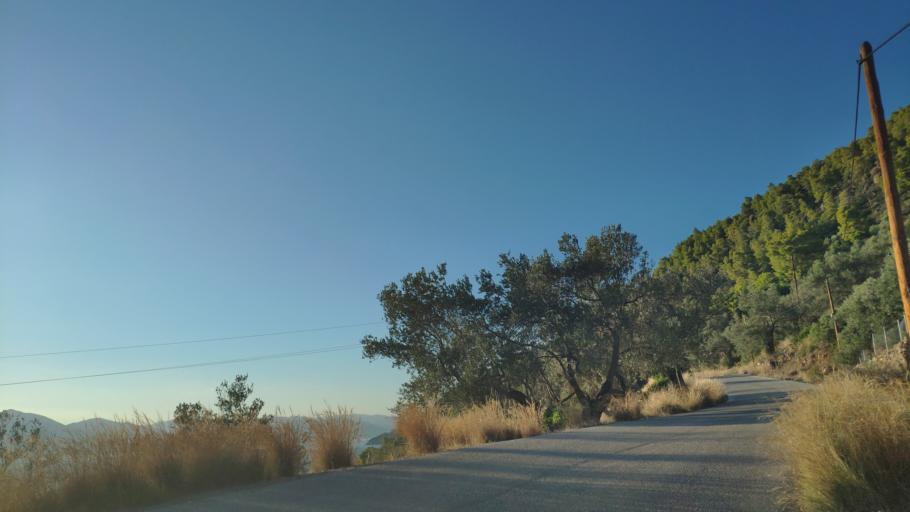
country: GR
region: Attica
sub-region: Nomos Piraios
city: Megalochori
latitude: 37.6001
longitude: 23.3360
